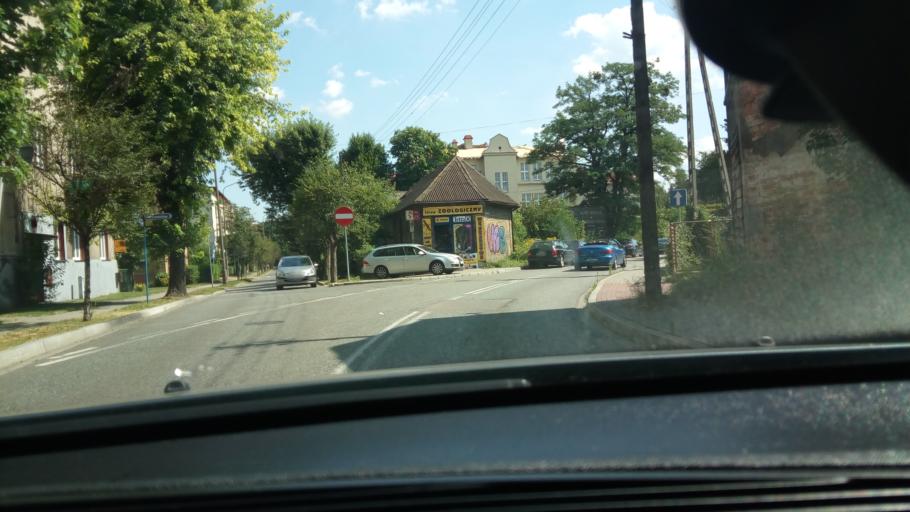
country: PL
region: Lesser Poland Voivodeship
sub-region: Powiat chrzanowski
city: Chrzanow
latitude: 50.1390
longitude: 19.3957
